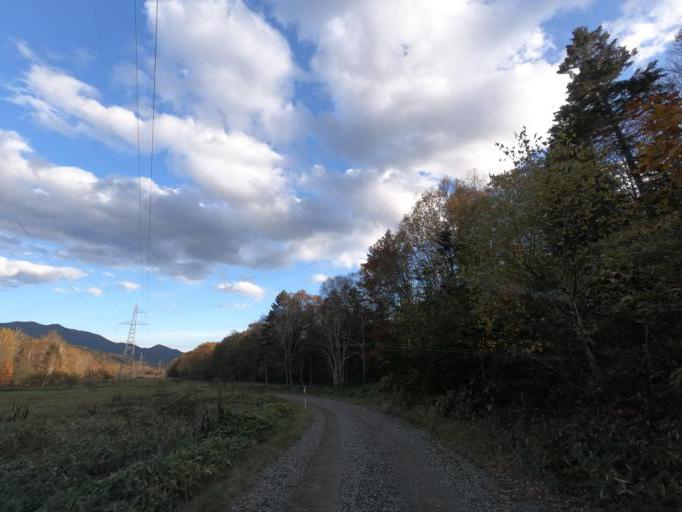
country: JP
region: Hokkaido
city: Otofuke
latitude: 43.4324
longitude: 143.1599
